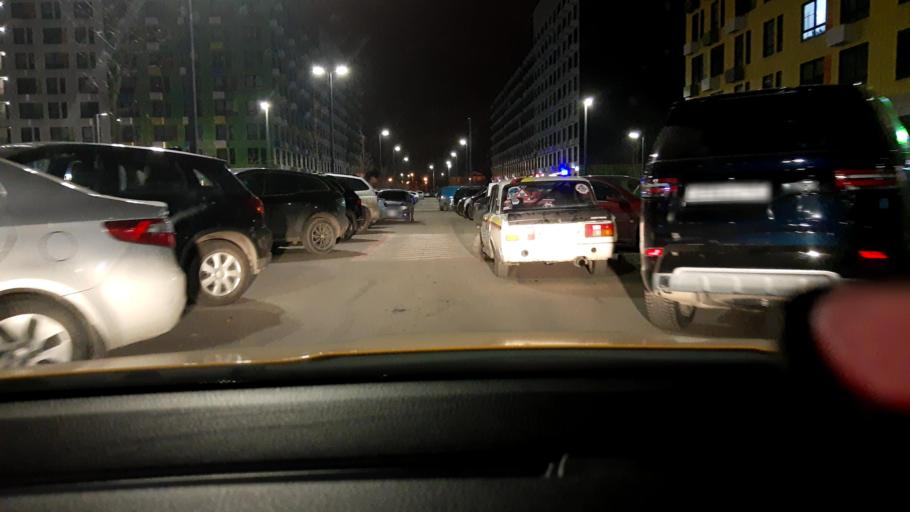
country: RU
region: Moskovskaya
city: Kommunarka
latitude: 55.5424
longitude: 37.4848
